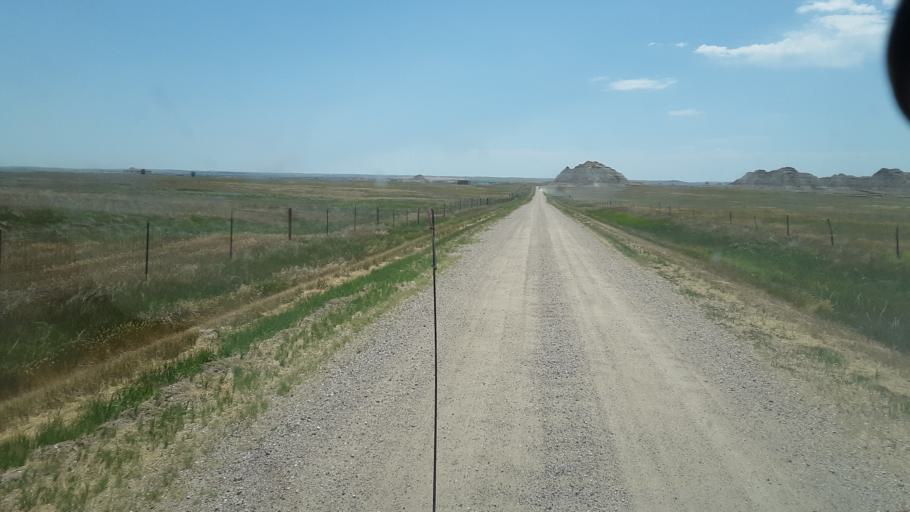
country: US
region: South Dakota
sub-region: Haakon County
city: Philip
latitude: 43.7446
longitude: -101.9995
